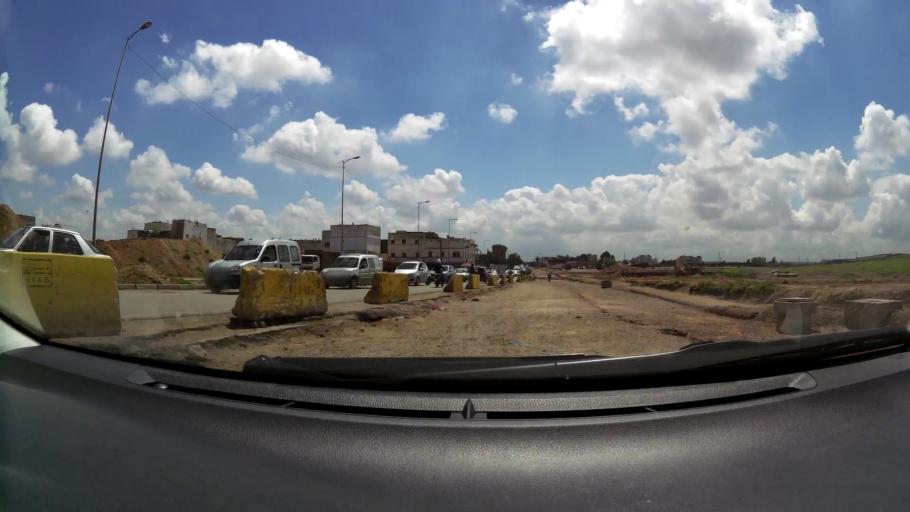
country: MA
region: Grand Casablanca
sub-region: Mediouna
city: Tit Mellil
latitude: 33.5432
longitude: -7.5432
